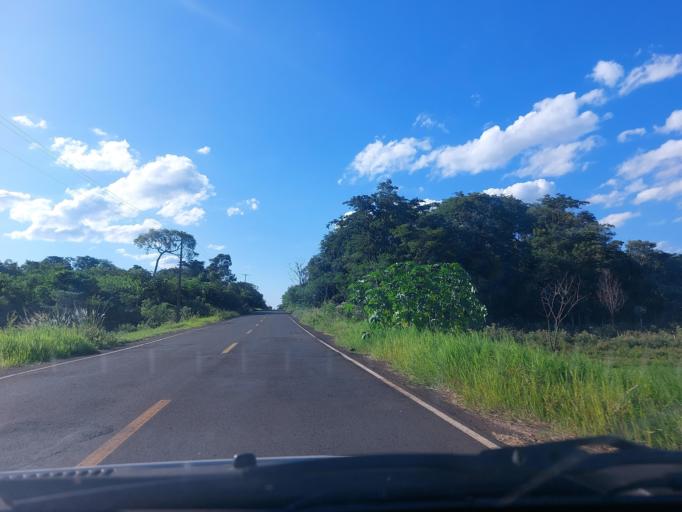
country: PY
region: San Pedro
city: Guayaybi
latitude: -24.5807
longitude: -56.5196
